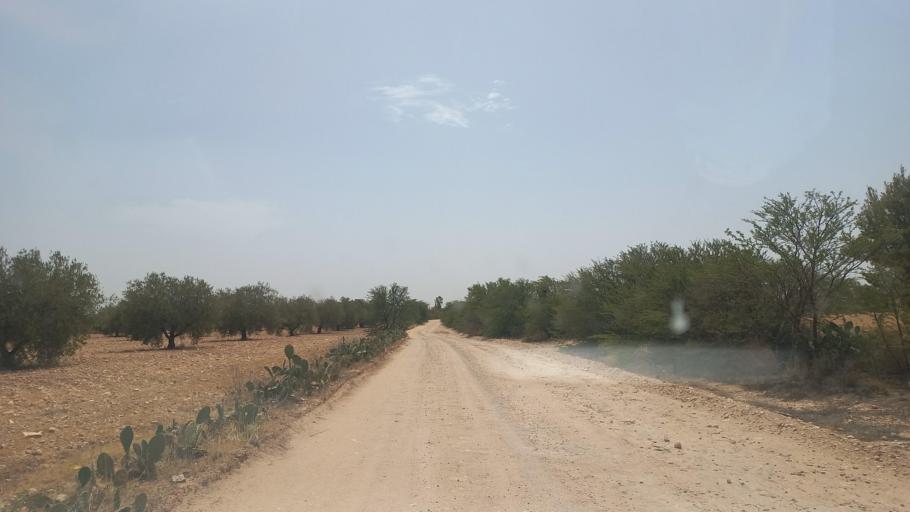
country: TN
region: Al Qasrayn
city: Kasserine
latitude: 35.2548
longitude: 9.0069
